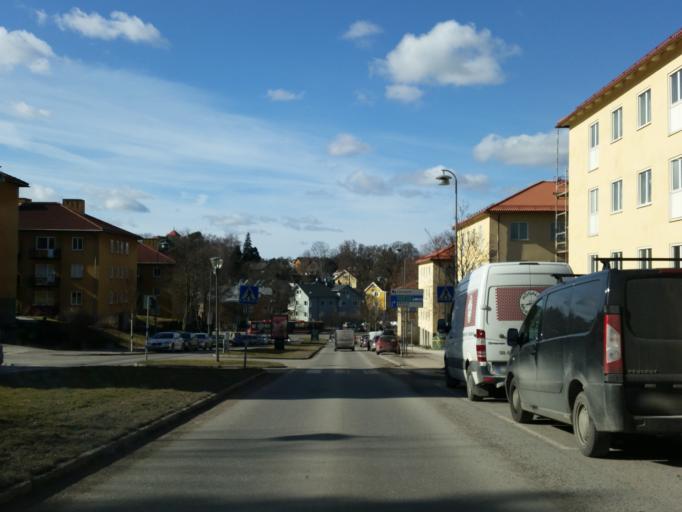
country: SE
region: Stockholm
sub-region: Sundbybergs Kommun
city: Sundbyberg
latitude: 59.3685
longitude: 17.9634
